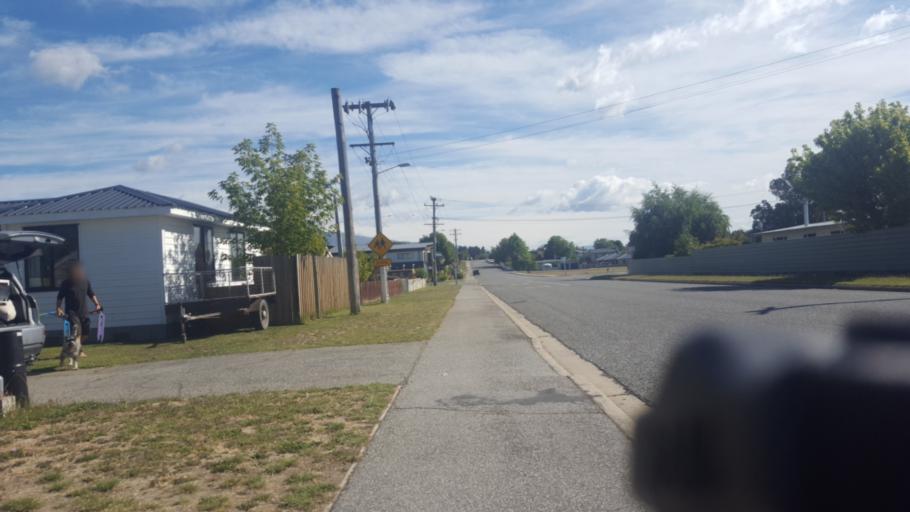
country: NZ
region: Otago
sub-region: Queenstown-Lakes District
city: Wanaka
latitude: -45.0483
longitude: 169.2034
